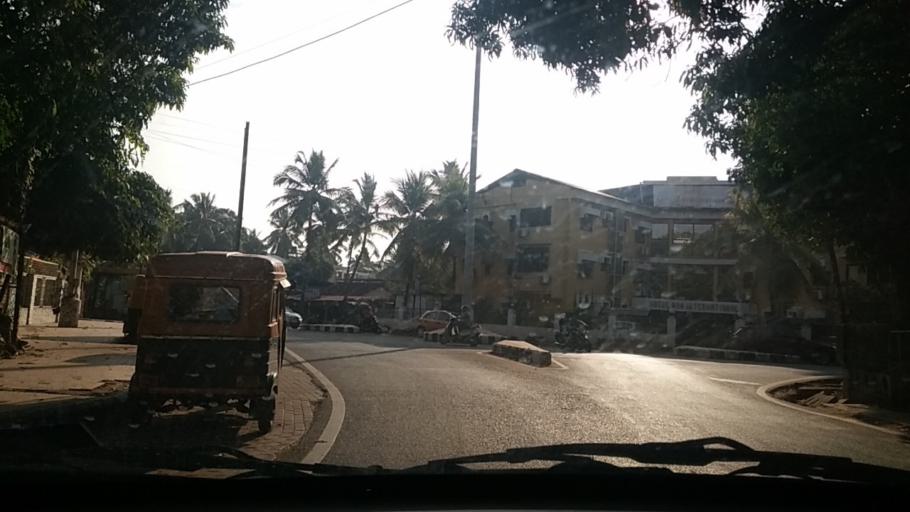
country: IN
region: Goa
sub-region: North Goa
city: Panaji
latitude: 15.4807
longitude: 73.8124
